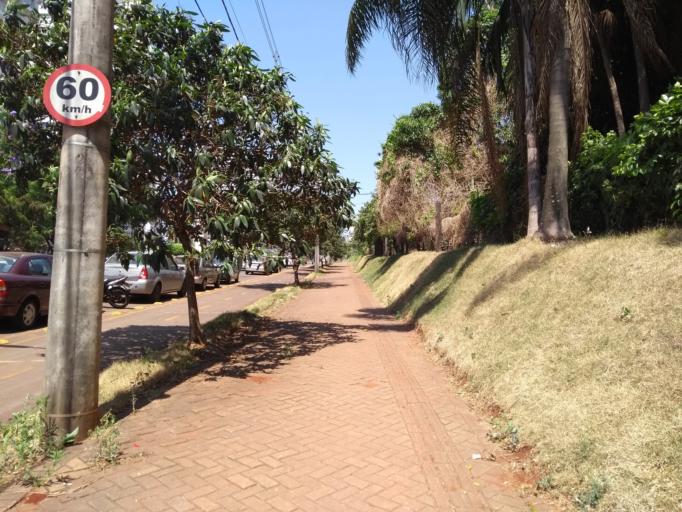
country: BR
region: Parana
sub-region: Londrina
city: Londrina
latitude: -23.3315
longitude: -51.1776
